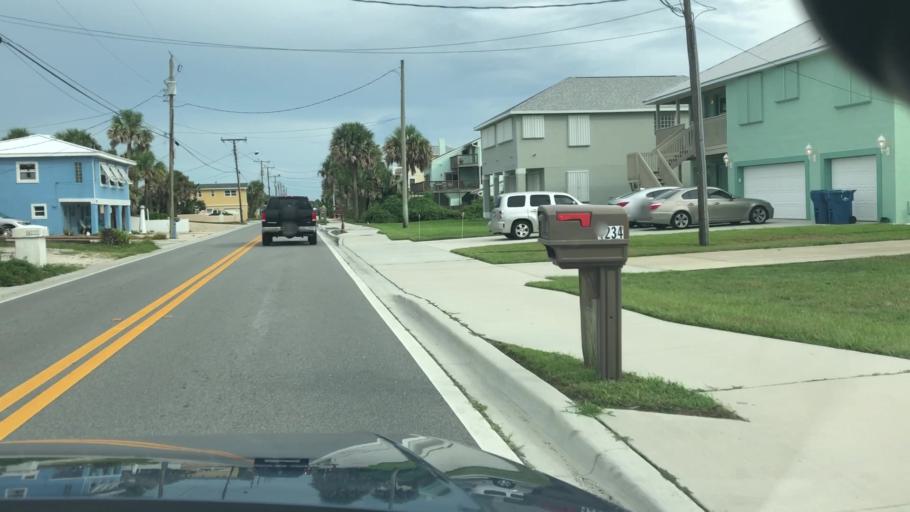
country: US
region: Florida
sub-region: Volusia County
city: Ponce Inlet
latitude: 29.1261
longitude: -80.9547
